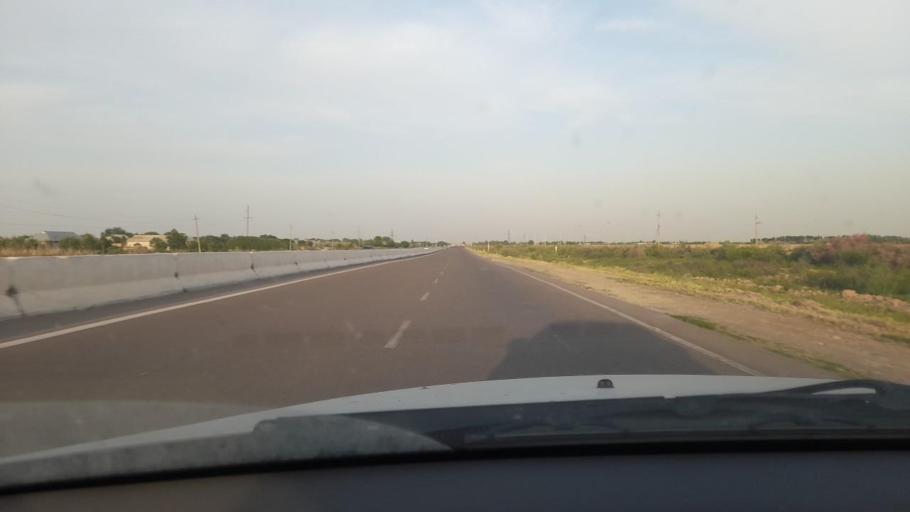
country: UZ
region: Sirdaryo
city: Guliston
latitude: 40.4933
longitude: 68.6705
